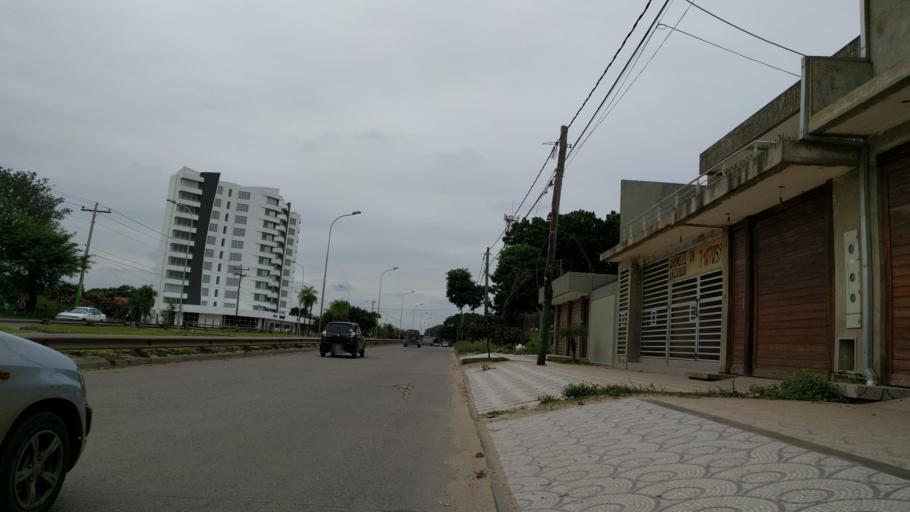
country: BO
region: Santa Cruz
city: Santa Cruz de la Sierra
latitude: -17.8003
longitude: -63.2223
